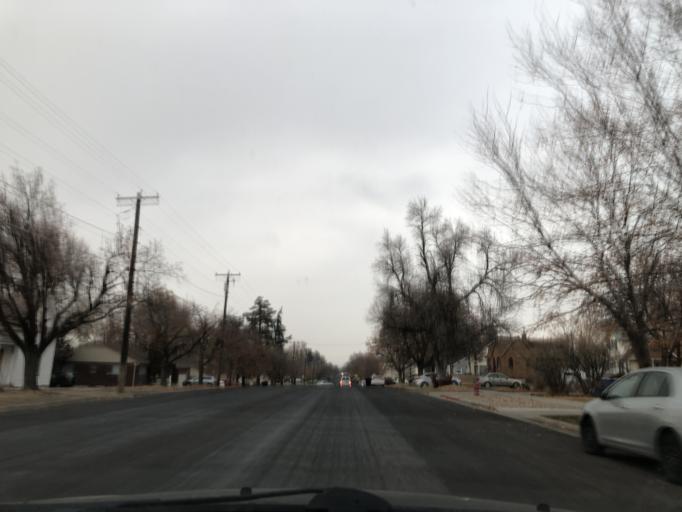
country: US
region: Utah
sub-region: Cache County
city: Logan
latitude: 41.7375
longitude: -111.8219
